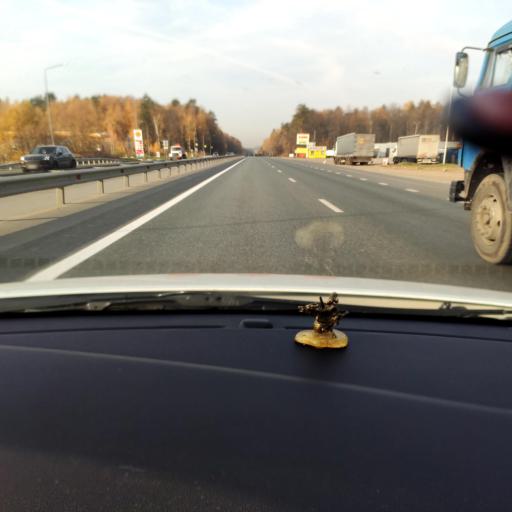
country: RU
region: Tatarstan
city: Staroye Arakchino
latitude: 55.9098
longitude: 49.0557
